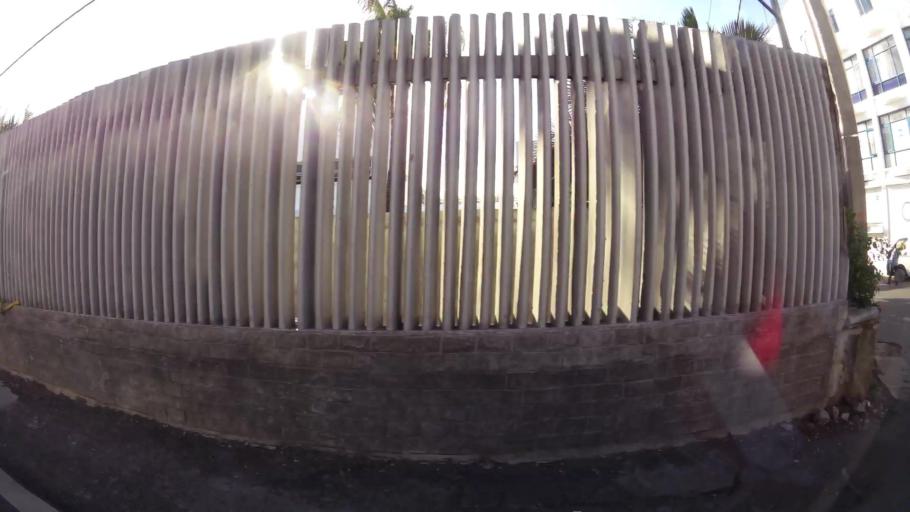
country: MU
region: Port Louis
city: Port Louis
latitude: -20.1689
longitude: 57.4833
